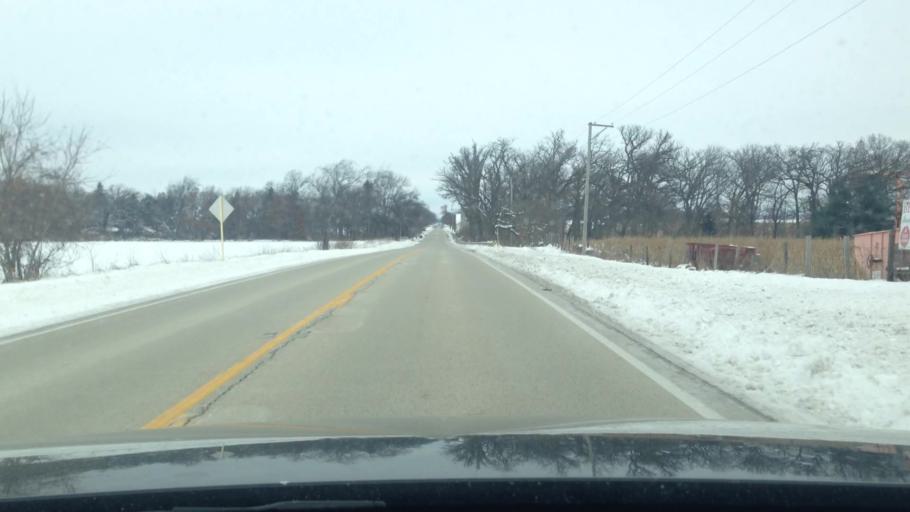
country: US
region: Illinois
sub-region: McHenry County
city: Hebron
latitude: 42.4043
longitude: -88.4382
